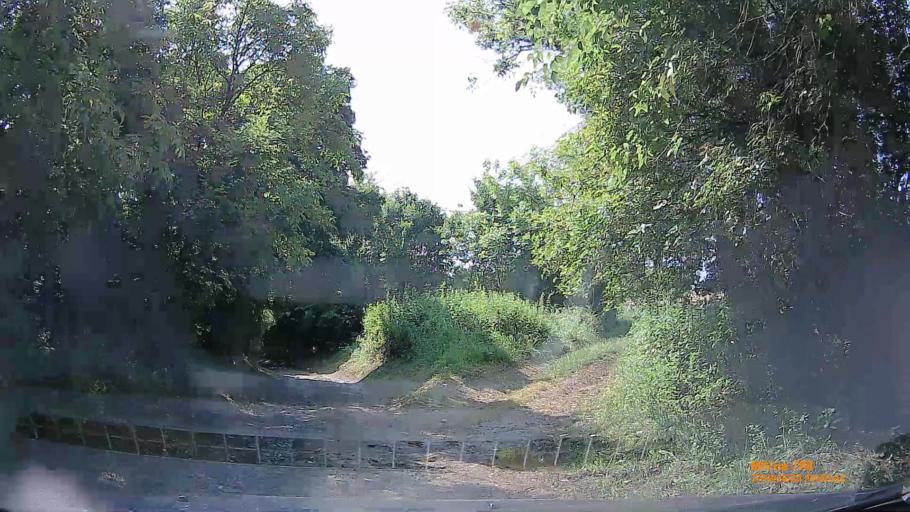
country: HU
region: Baranya
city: Mecseknadasd
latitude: 46.1790
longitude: 18.4811
